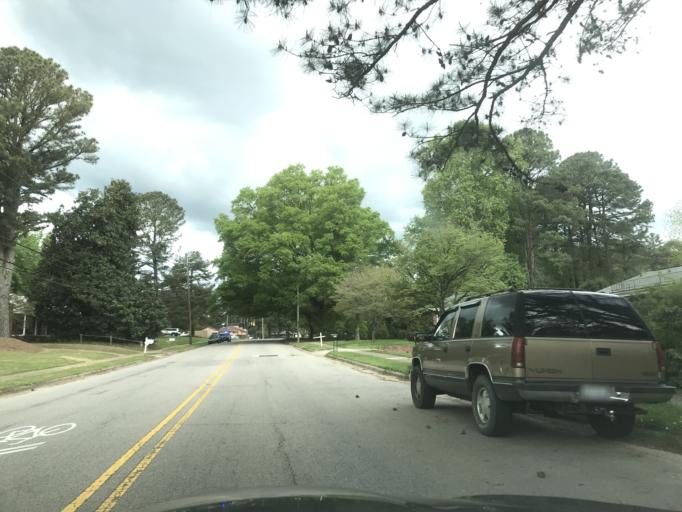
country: US
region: North Carolina
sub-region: Wake County
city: West Raleigh
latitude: 35.7775
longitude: -78.7202
